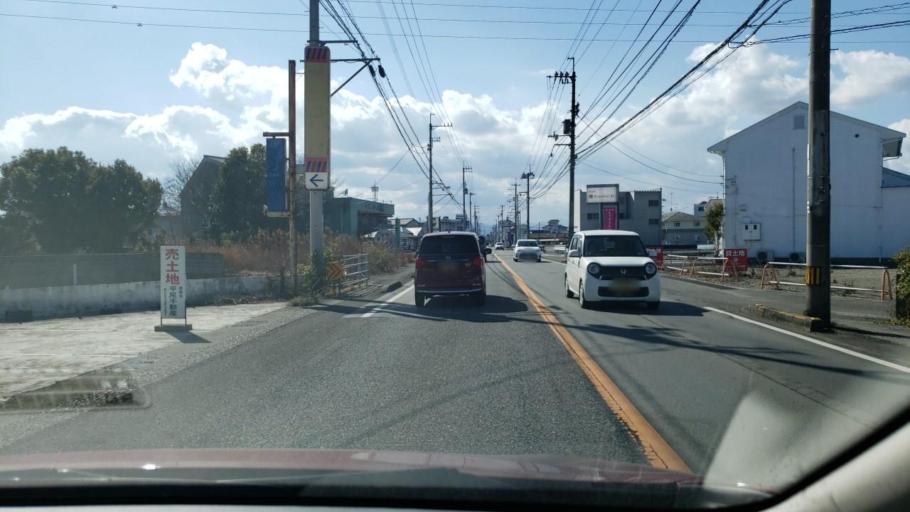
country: JP
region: Tokushima
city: Ishii
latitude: 34.1338
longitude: 134.4908
